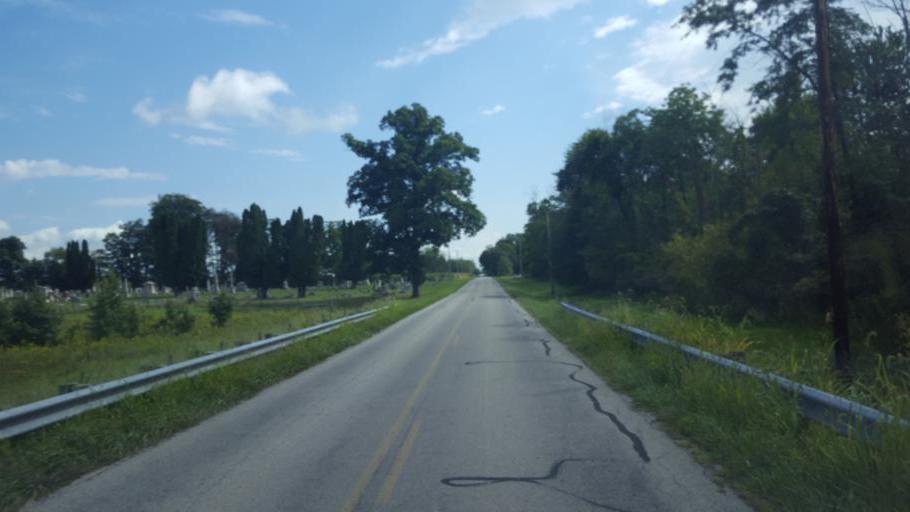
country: US
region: Ohio
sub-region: Seneca County
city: Tiffin
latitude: 41.0661
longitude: -83.0958
